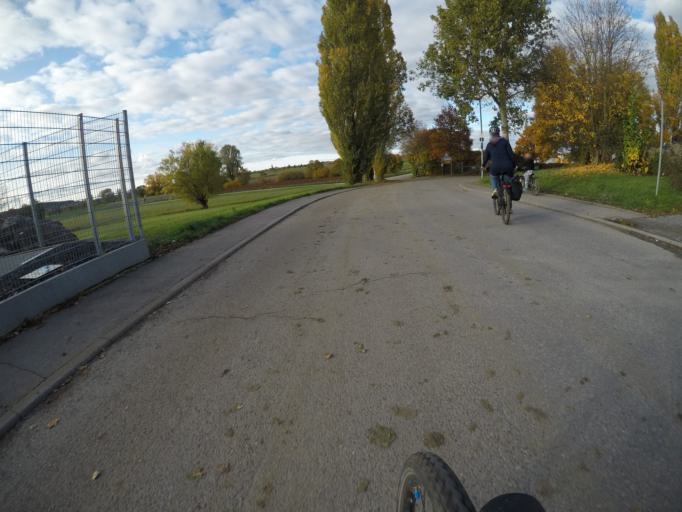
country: DE
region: Baden-Wuerttemberg
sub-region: Regierungsbezirk Stuttgart
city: Leinfelden-Echterdingen
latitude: 48.6745
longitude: 9.1823
